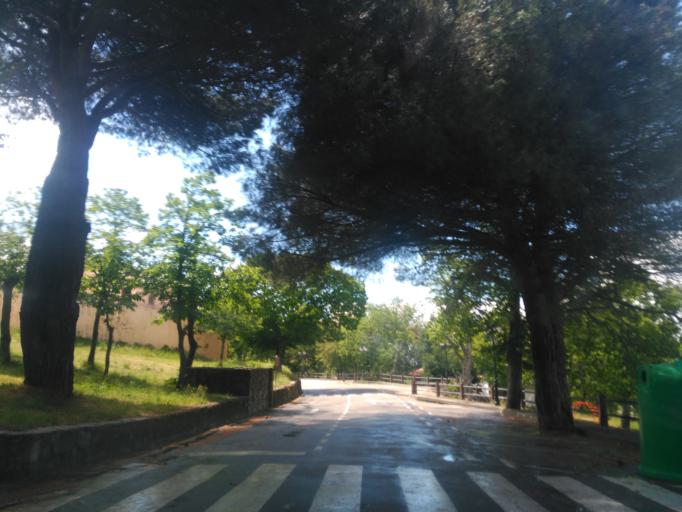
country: ES
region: Castille and Leon
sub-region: Provincia de Salamanca
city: Bejar
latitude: 40.3792
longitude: -5.7612
